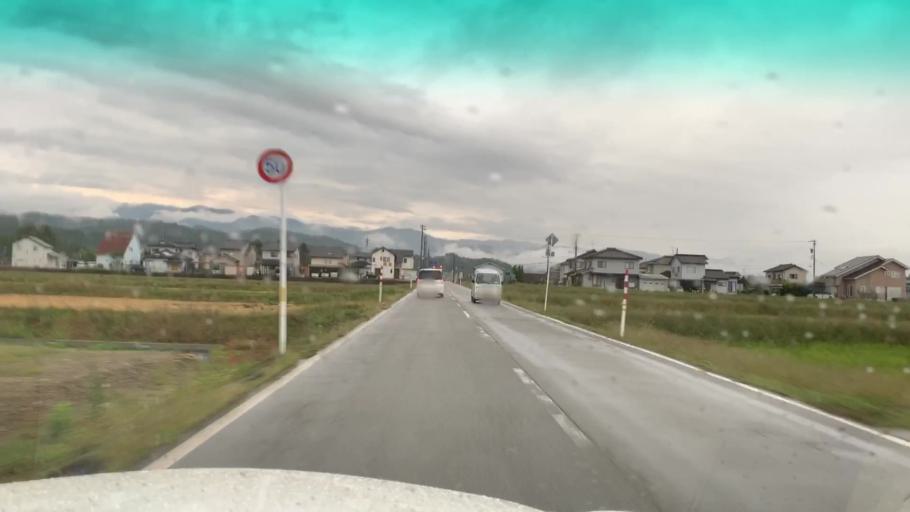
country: JP
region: Toyama
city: Kamiichi
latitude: 36.6328
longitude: 137.3286
